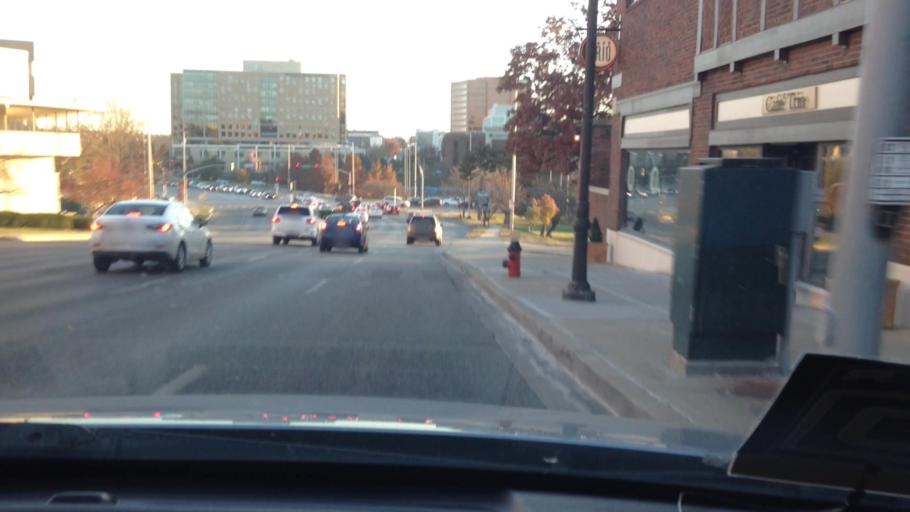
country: US
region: Kansas
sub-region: Johnson County
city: Westwood
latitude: 39.0438
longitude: -94.5869
